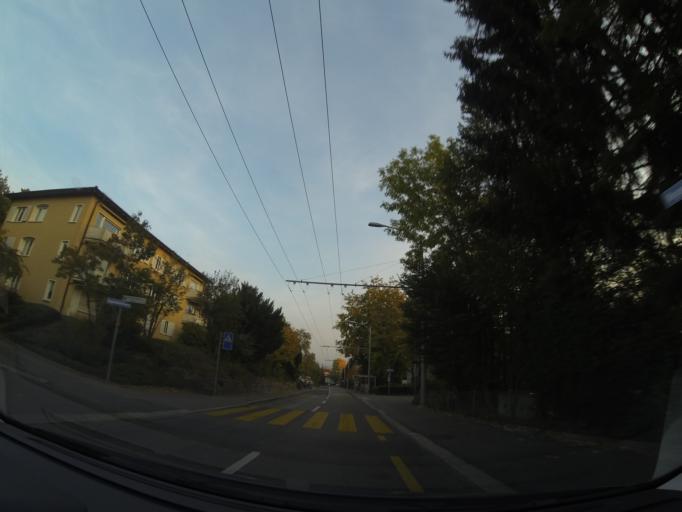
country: CH
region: Zurich
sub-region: Bezirk Zuerich
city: Zuerich (Kreis 10) / Hoengg
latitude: 47.4077
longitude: 8.4897
